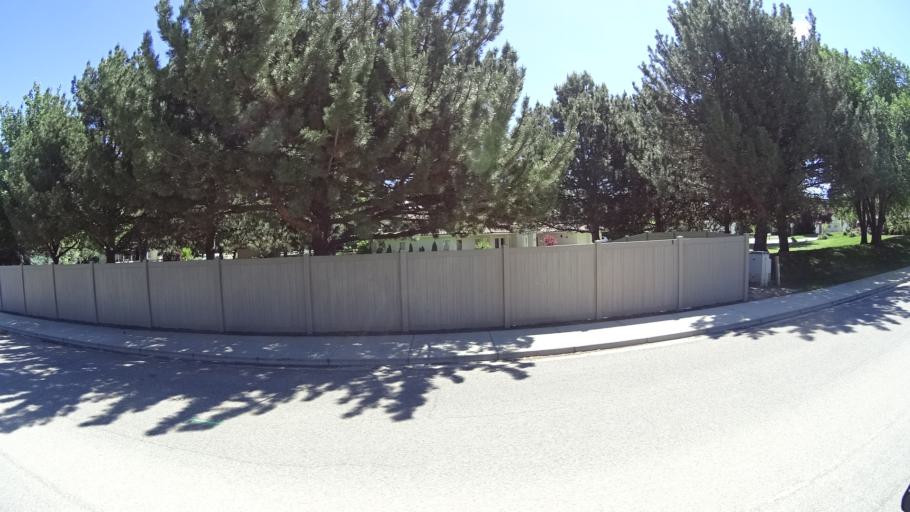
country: US
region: Idaho
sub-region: Ada County
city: Eagle
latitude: 43.6645
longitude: -116.3745
